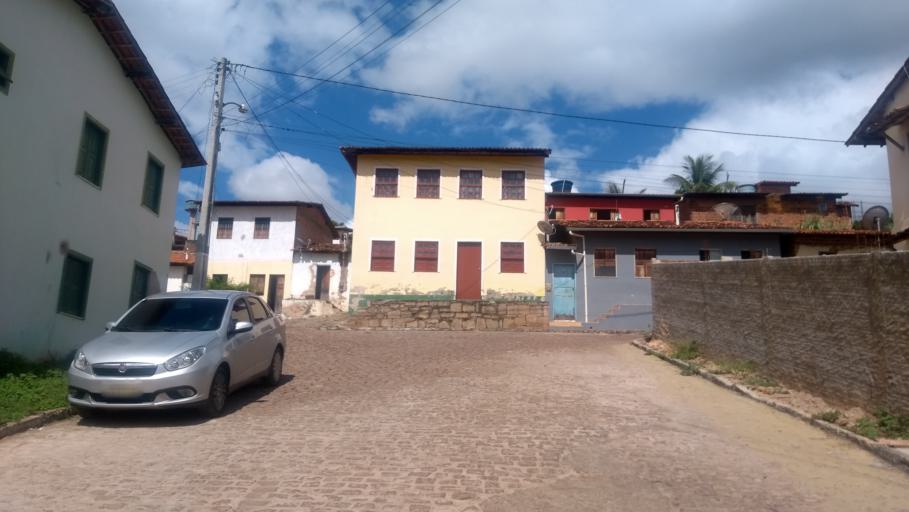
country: BR
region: Bahia
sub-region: Andarai
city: Vera Cruz
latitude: -12.5664
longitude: -41.3899
